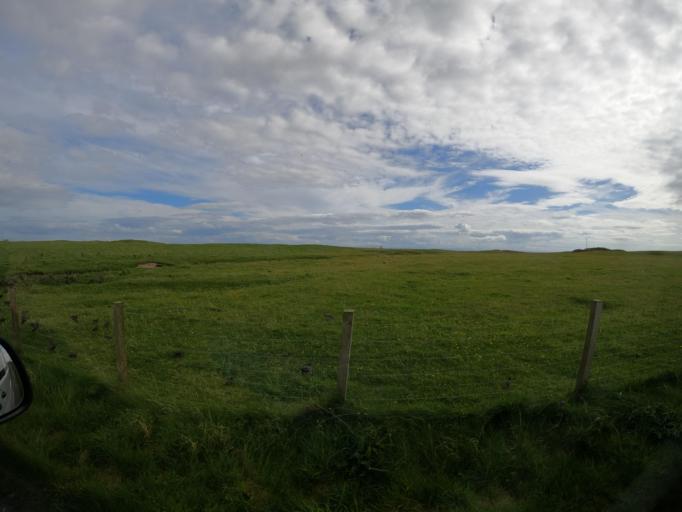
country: GB
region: Scotland
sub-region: Eilean Siar
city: Barra
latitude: 56.4791
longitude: -6.8997
